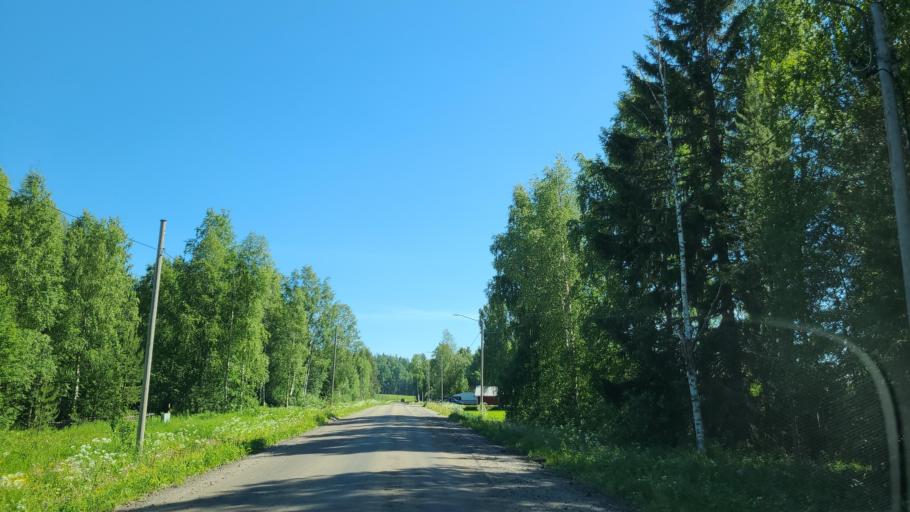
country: SE
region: Vaesterbotten
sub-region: Bjurholms Kommun
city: Bjurholm
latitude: 63.6968
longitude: 18.9517
